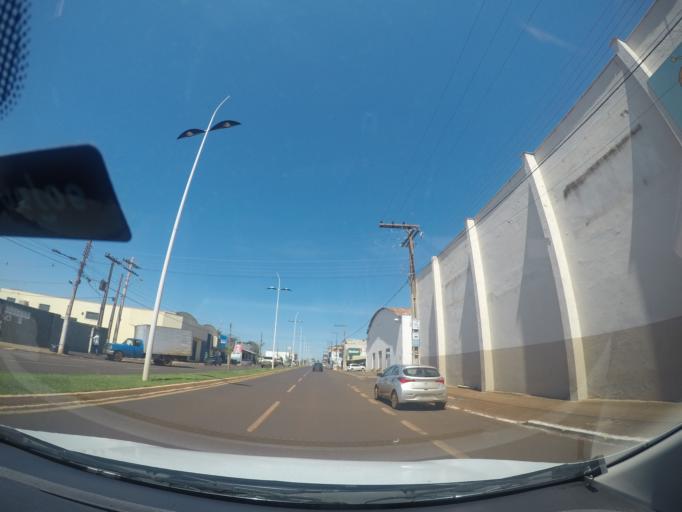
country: BR
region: Goias
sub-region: Itumbiara
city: Itumbiara
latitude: -18.4030
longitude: -49.2071
